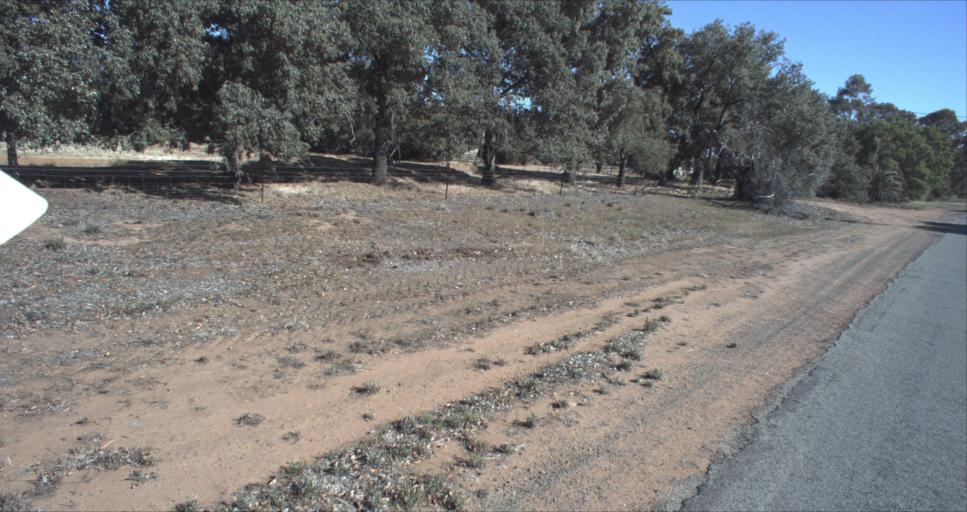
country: AU
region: New South Wales
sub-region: Leeton
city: Leeton
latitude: -34.5759
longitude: 146.3097
